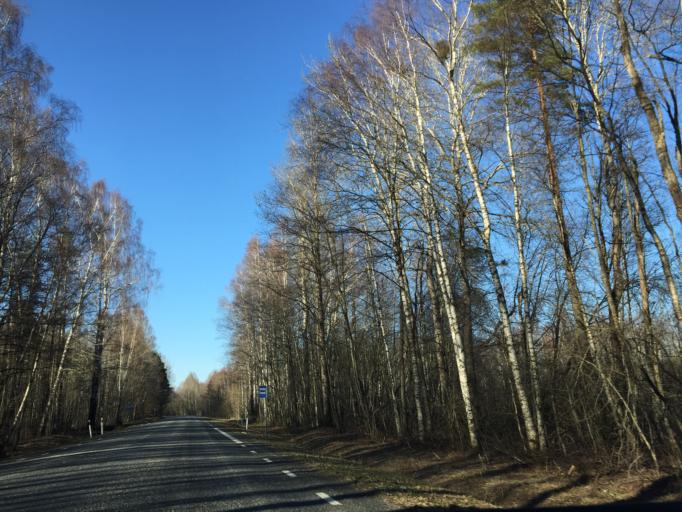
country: RU
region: Pskov
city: Gdov
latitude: 59.0269
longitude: 27.6867
